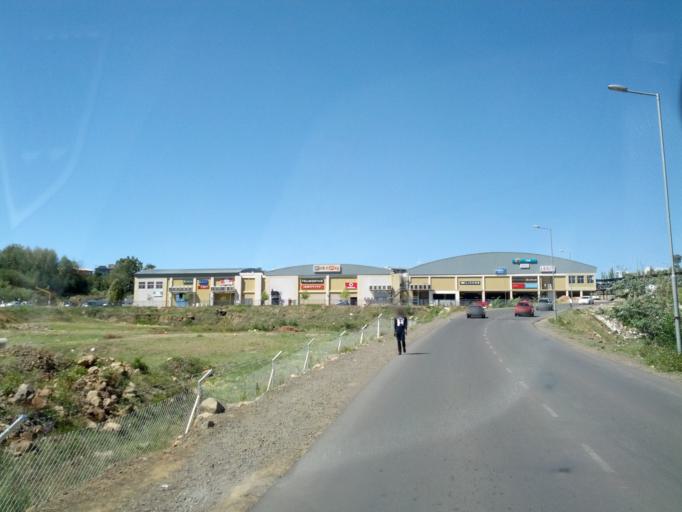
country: LS
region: Maseru
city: Maseru
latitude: -29.3186
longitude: 27.4760
